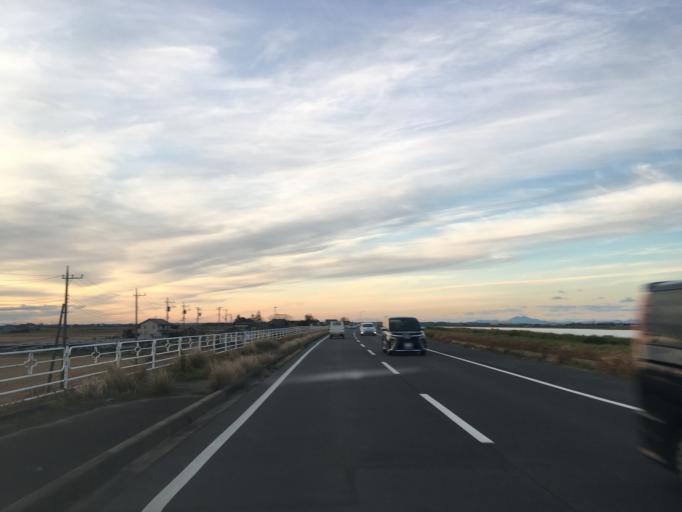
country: JP
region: Chiba
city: Katori-shi
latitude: 35.9085
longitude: 140.4812
